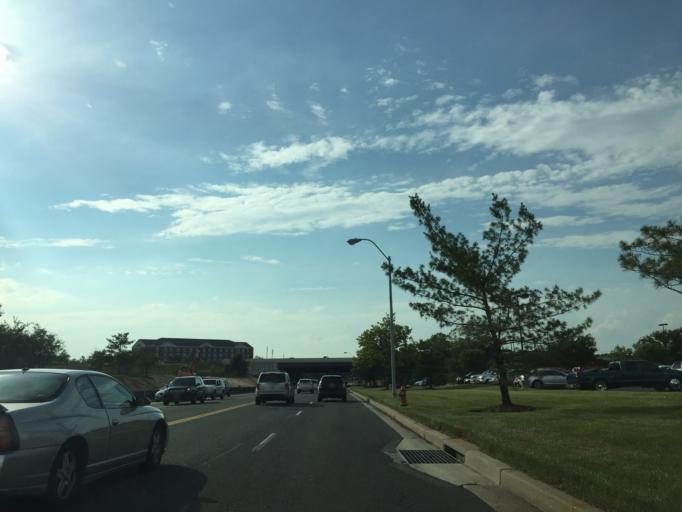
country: US
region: Maryland
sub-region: Baltimore County
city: White Marsh
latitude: 39.3707
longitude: -76.4550
